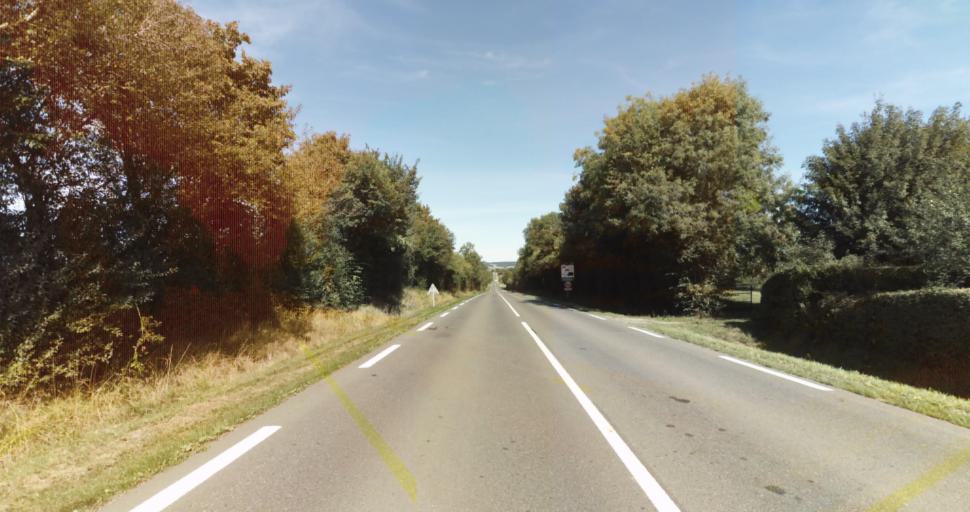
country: FR
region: Lower Normandy
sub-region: Departement de l'Orne
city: Gace
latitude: 48.7377
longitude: 0.2584
